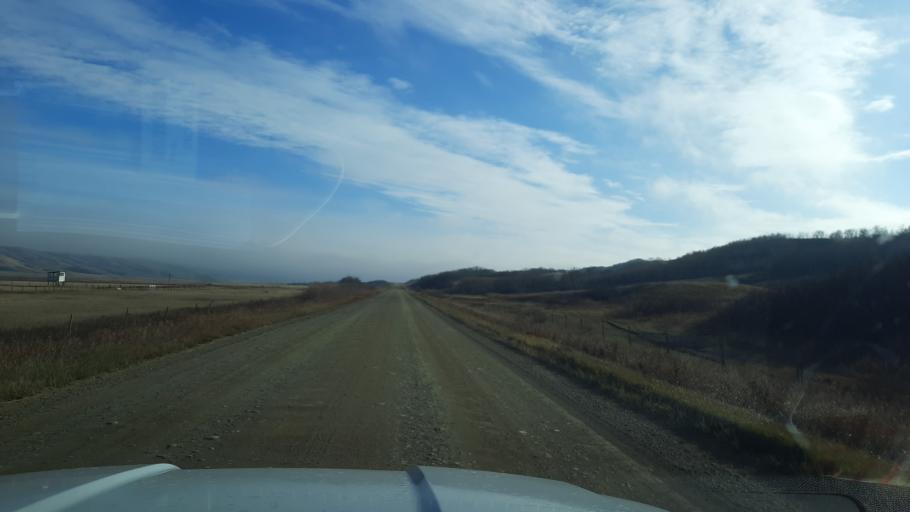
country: CA
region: Saskatchewan
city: Pilot Butte
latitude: 50.7837
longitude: -104.2430
